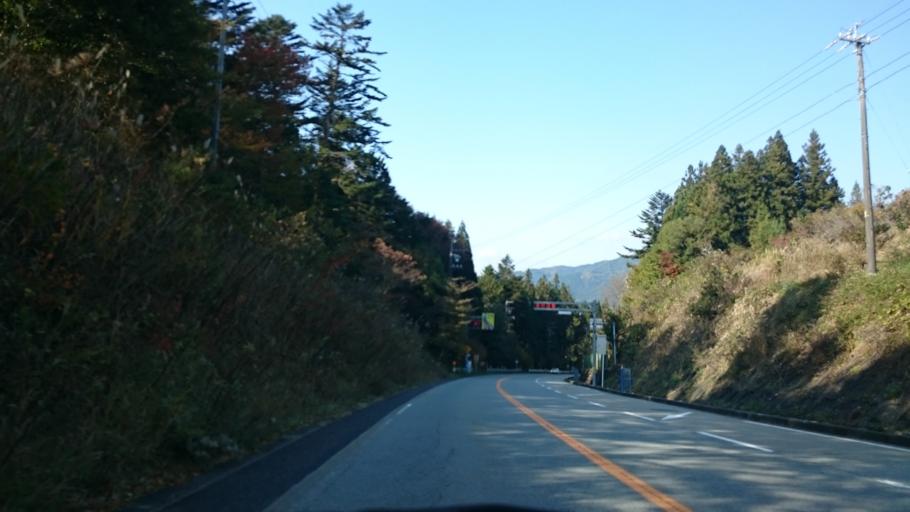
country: JP
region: Gifu
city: Nakatsugawa
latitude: 35.7512
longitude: 137.3284
